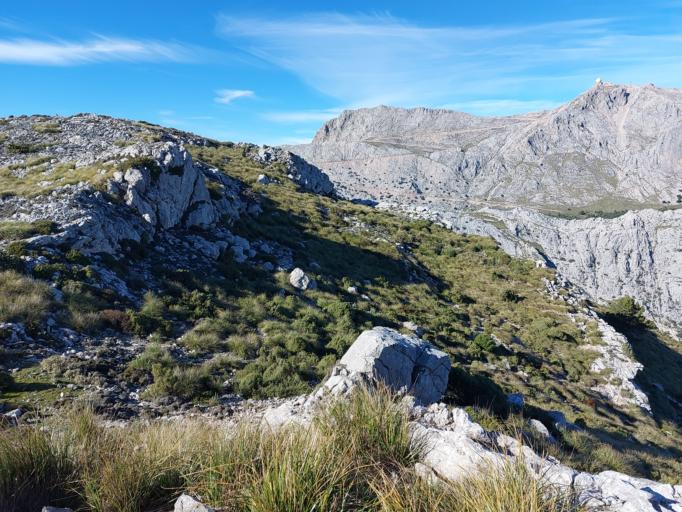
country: ES
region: Balearic Islands
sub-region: Illes Balears
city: Escorca
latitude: 39.7870
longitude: 2.8100
